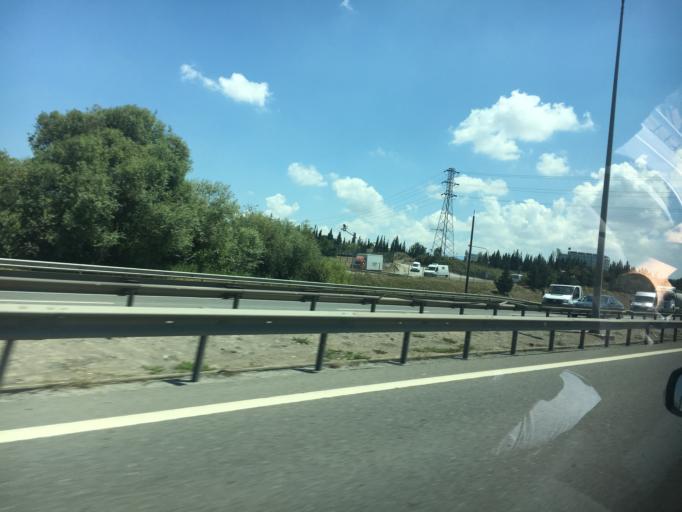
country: TR
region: Kocaeli
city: Balcik
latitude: 40.8895
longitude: 29.3728
